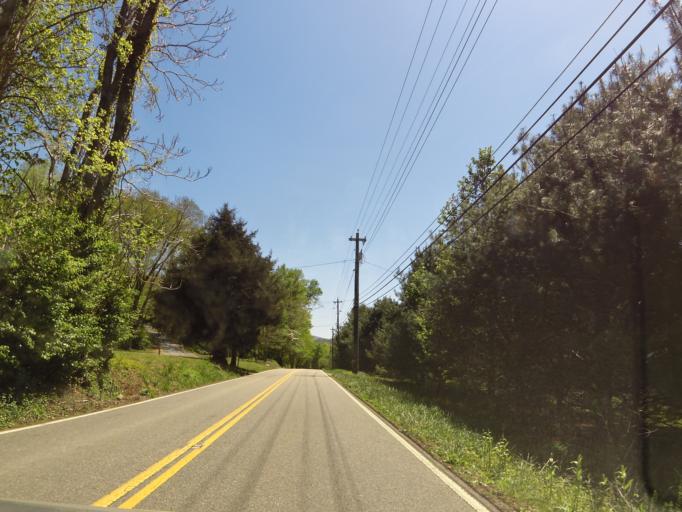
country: US
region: Tennessee
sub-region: Unicoi County
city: Erwin
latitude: 36.1679
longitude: -82.4437
